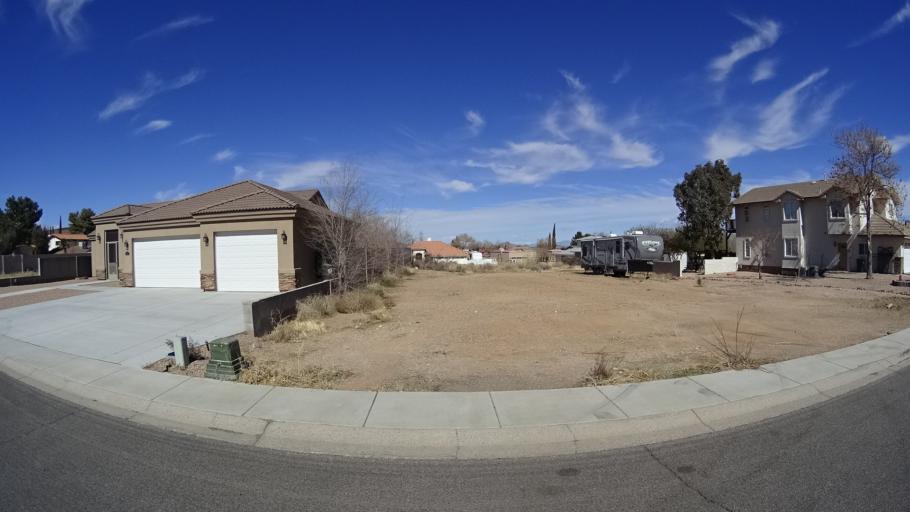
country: US
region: Arizona
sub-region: Mohave County
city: Kingman
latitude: 35.2095
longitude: -114.0478
